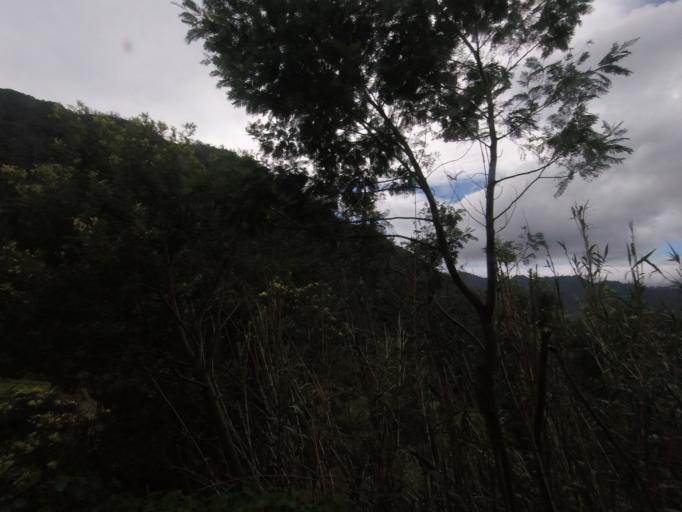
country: PT
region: Madeira
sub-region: Machico
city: Canical
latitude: 32.7628
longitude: -16.8086
